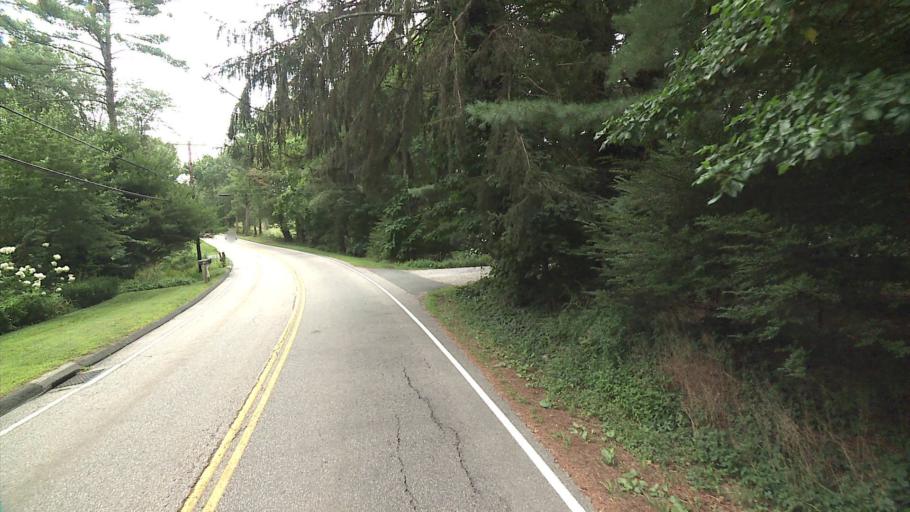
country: US
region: Connecticut
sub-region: Middlesex County
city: Essex Village
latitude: 41.3720
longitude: -72.3475
